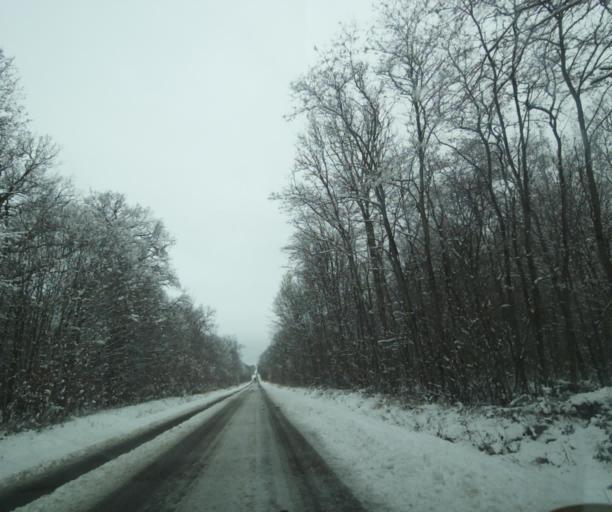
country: FR
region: Champagne-Ardenne
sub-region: Departement de la Haute-Marne
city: Montier-en-Der
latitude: 48.5171
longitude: 4.7471
